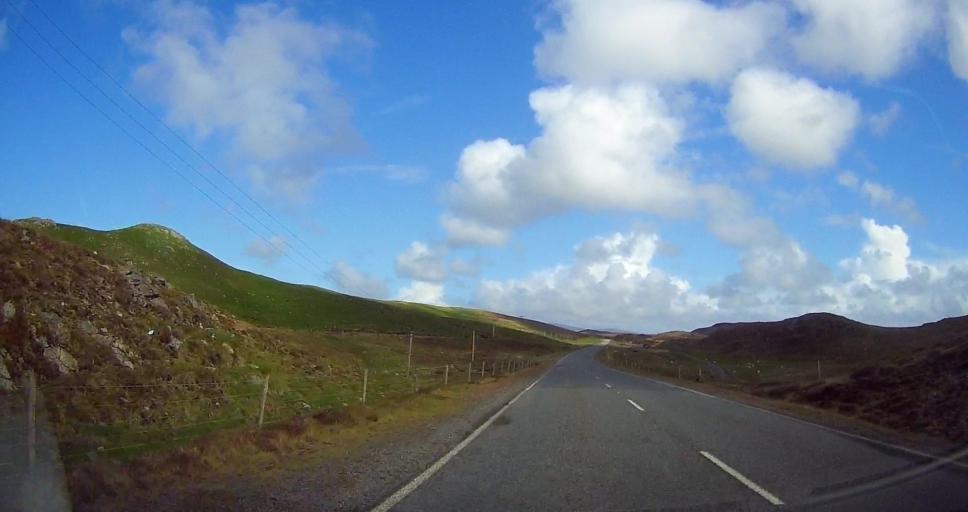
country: GB
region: Scotland
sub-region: Shetland Islands
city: Lerwick
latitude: 60.4240
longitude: -1.3955
